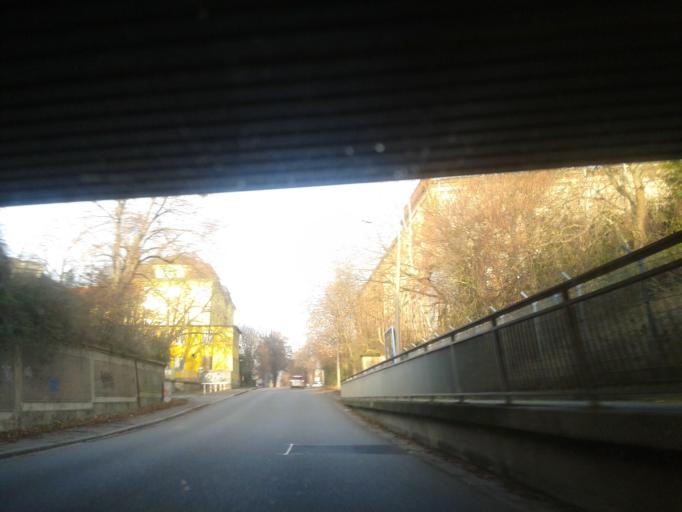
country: DE
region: Saxony
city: Heidenau
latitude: 51.0037
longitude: 13.8218
